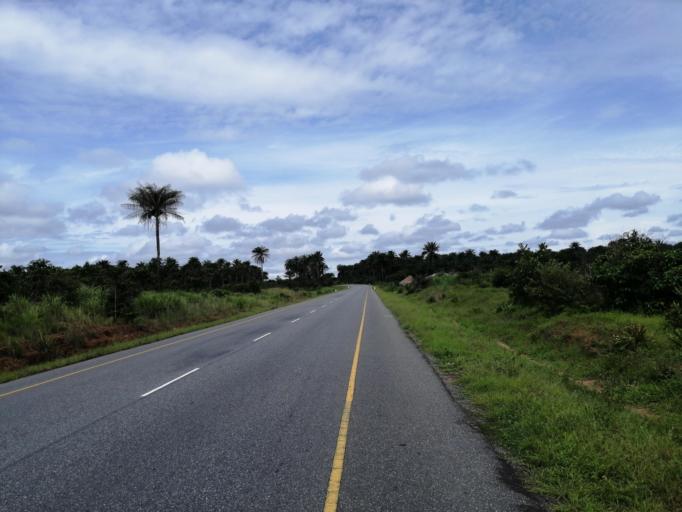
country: SL
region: Northern Province
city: Pepel
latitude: 8.7217
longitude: -12.9580
